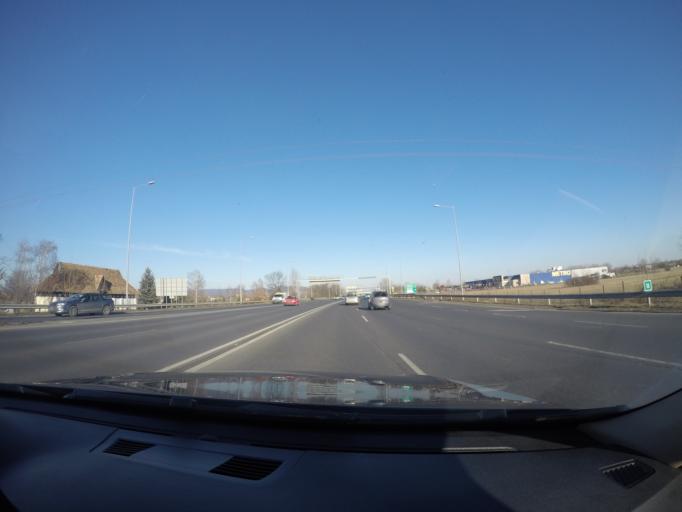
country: HU
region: Pest
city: Budakalasz
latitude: 47.6153
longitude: 19.0653
